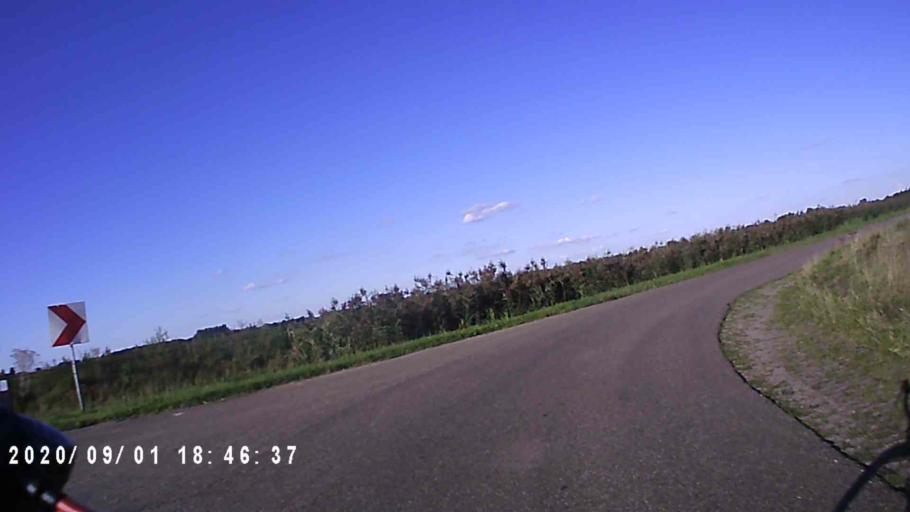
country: NL
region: Groningen
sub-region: Gemeente Veendam
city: Veendam
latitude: 53.1481
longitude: 6.8476
